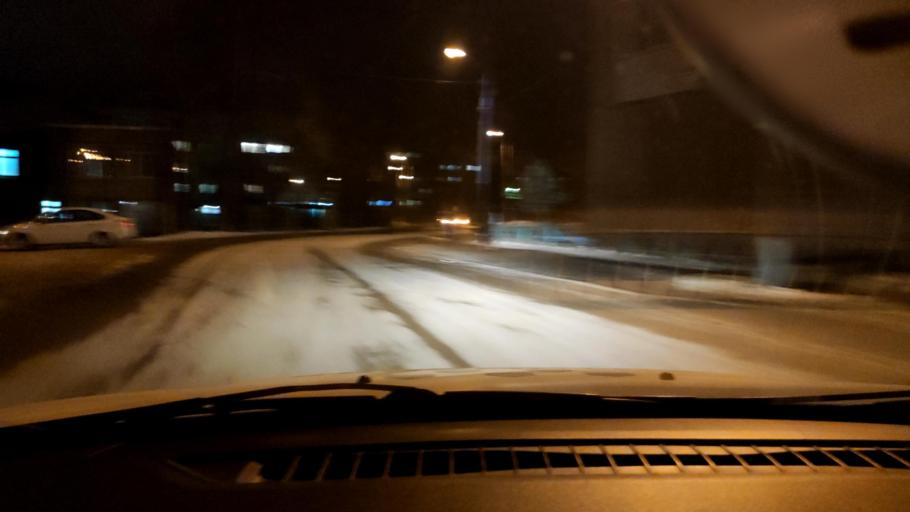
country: RU
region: Perm
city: Kultayevo
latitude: 57.9987
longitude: 55.9356
